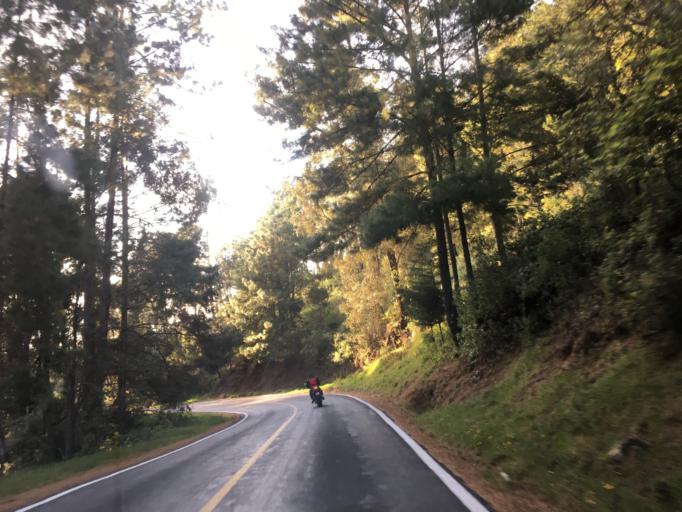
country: MX
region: Michoacan
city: Tzitzio
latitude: 19.6813
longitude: -100.8847
